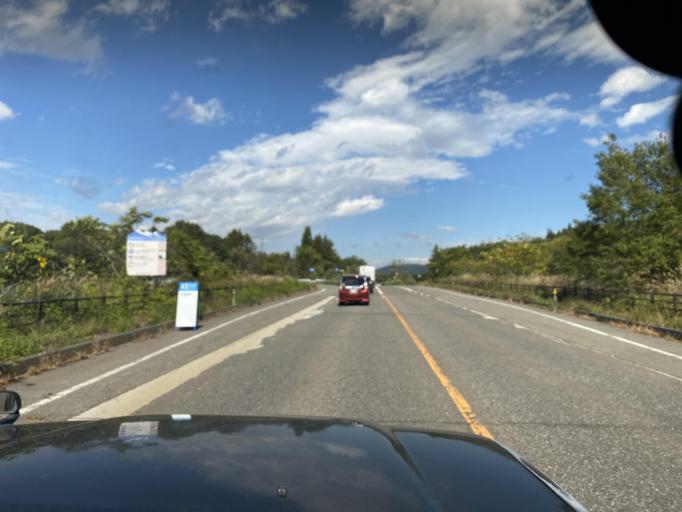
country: JP
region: Nagano
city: Omachi
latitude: 36.5977
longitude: 137.8468
